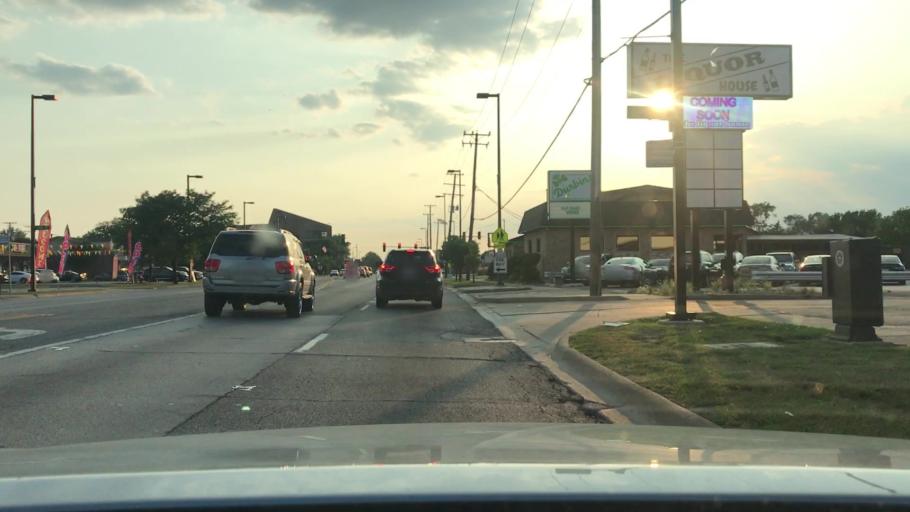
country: US
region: Illinois
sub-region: Cook County
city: Hometown
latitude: 41.7489
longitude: -87.7556
